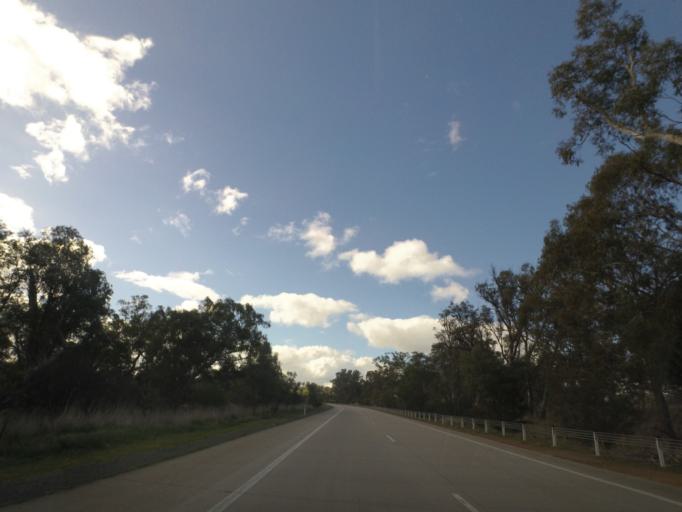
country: AU
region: New South Wales
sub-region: Greater Hume Shire
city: Holbrook
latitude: -35.8729
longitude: 147.1832
